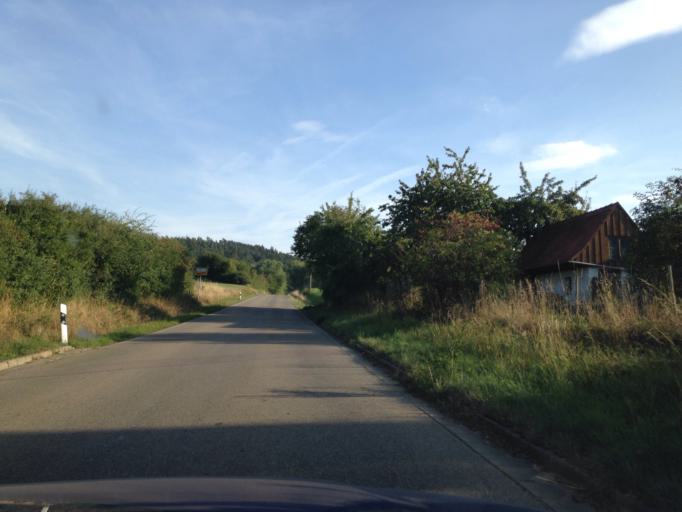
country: DE
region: Bavaria
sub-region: Regierungsbezirk Mittelfranken
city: Thalmassing
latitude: 49.1269
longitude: 11.2110
